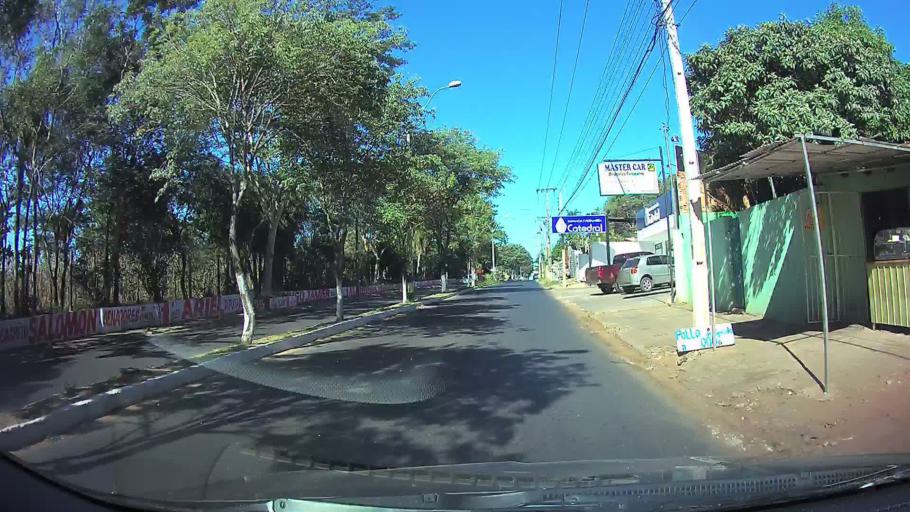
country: PY
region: Central
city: Villa Elisa
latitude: -25.3686
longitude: -57.5786
